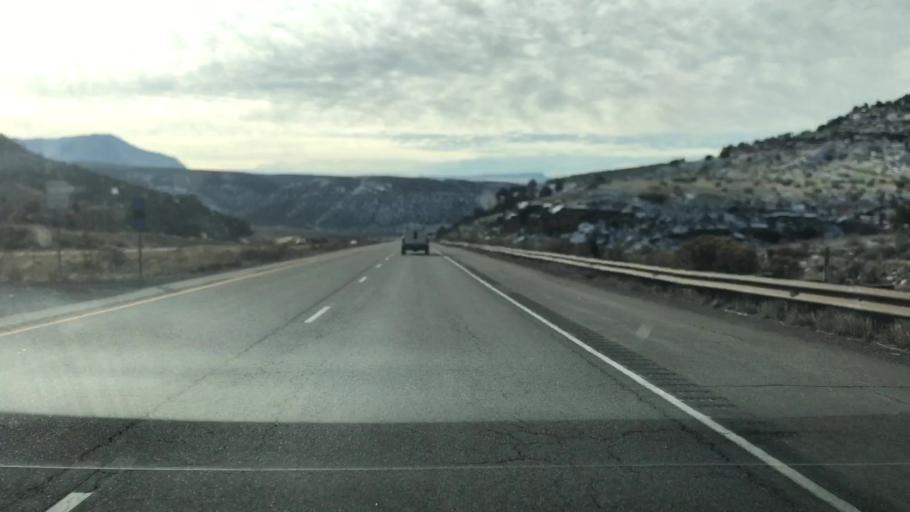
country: US
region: Colorado
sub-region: Garfield County
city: Parachute
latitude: 39.3658
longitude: -108.1702
